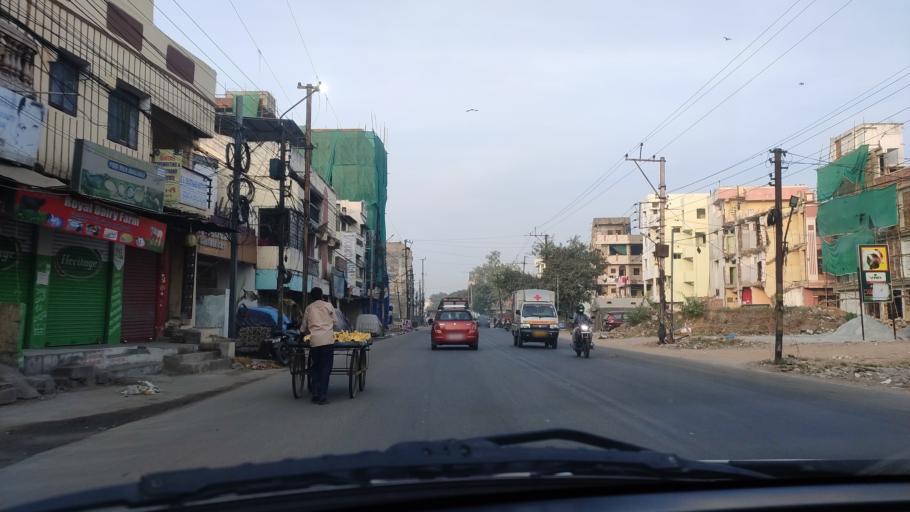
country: IN
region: Telangana
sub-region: Rangareddi
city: Gaddi Annaram
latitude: 17.3924
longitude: 78.5188
